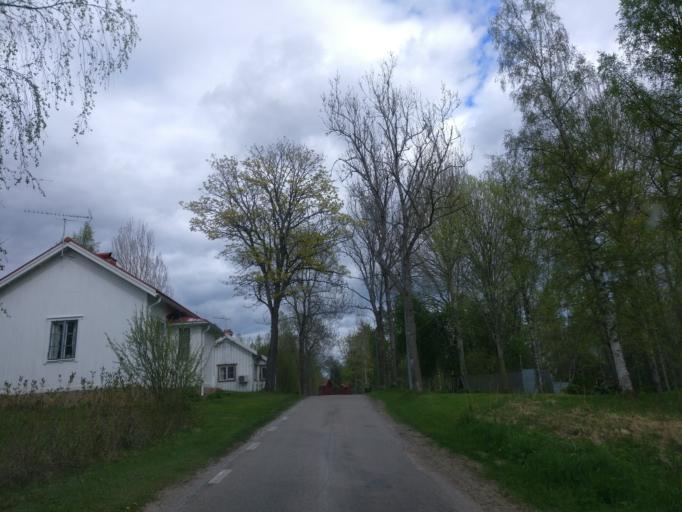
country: SE
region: Gaevleborg
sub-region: Soderhamns Kommun
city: Marielund
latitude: 61.4602
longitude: 17.1275
